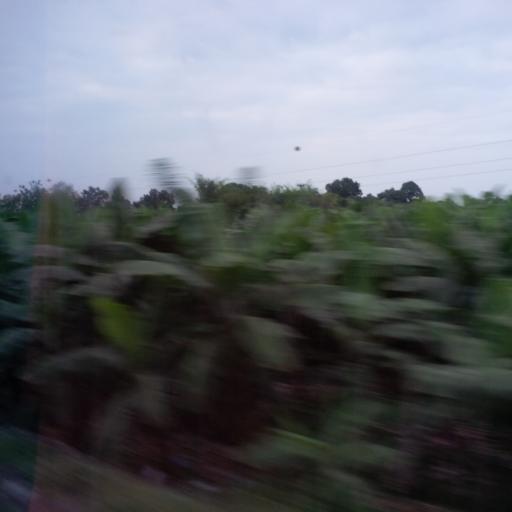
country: EC
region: Canar
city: La Troncal
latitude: -2.3436
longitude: -79.3728
